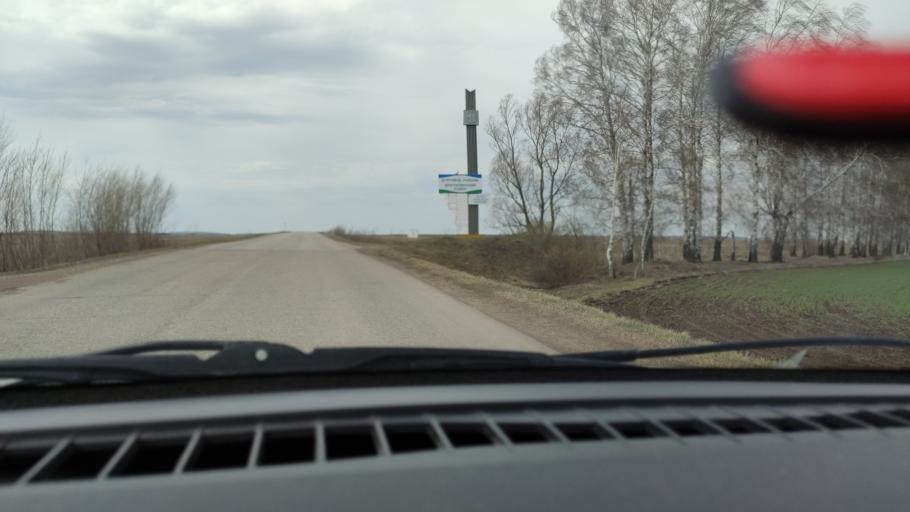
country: RU
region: Bashkortostan
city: Dyurtyuli
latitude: 55.6604
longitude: 55.0537
